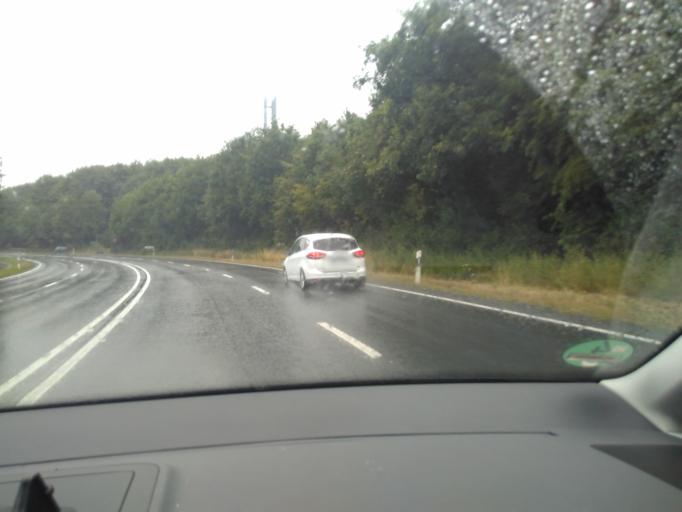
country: DE
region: North Rhine-Westphalia
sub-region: Regierungsbezirk Detmold
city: Bielefeld
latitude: 52.0408
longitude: 8.6096
